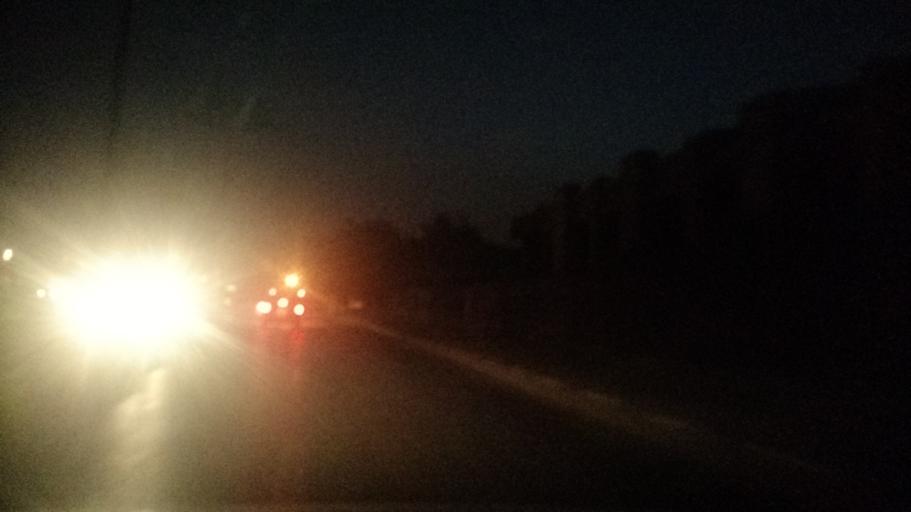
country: EG
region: Muhafazat al Qahirah
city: Cairo
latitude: 30.0202
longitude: 31.2742
